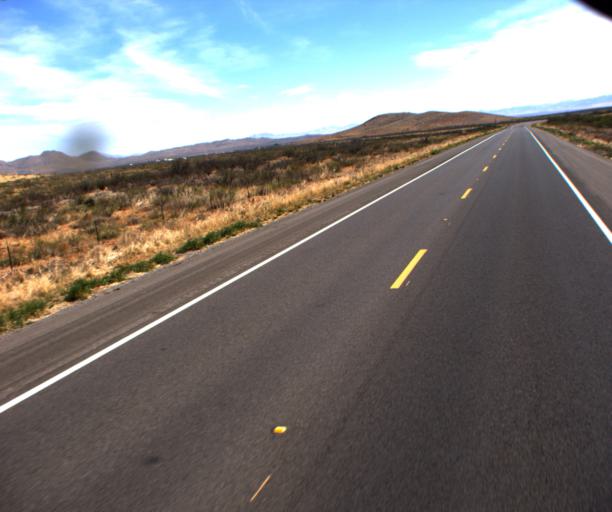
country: US
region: Arizona
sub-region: Cochise County
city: Tombstone
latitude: 31.9044
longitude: -109.7896
